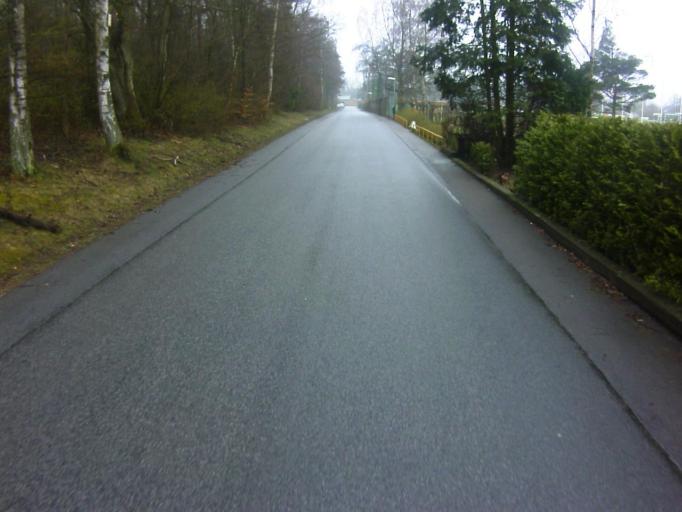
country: SE
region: Skane
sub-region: Kavlinge Kommun
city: Kaevlinge
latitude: 55.7775
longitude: 13.0886
